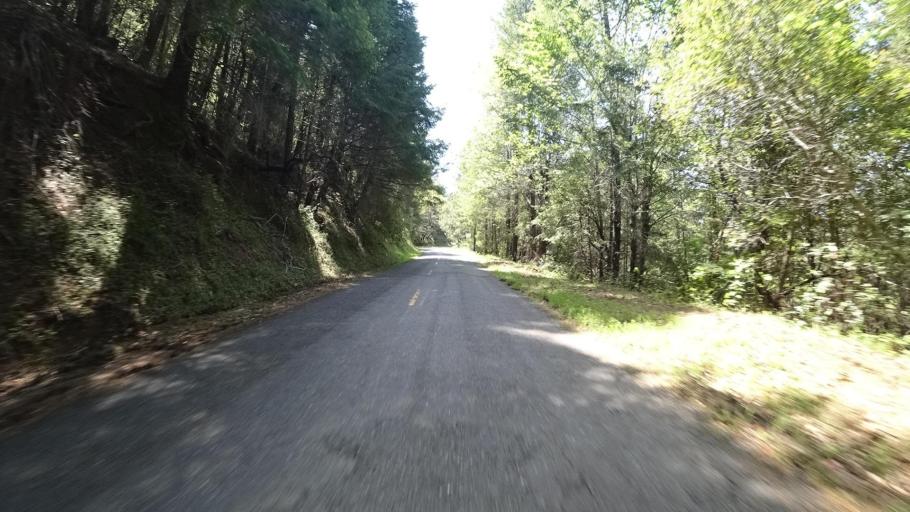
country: US
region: California
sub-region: Humboldt County
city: Redway
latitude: 40.2321
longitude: -123.6462
